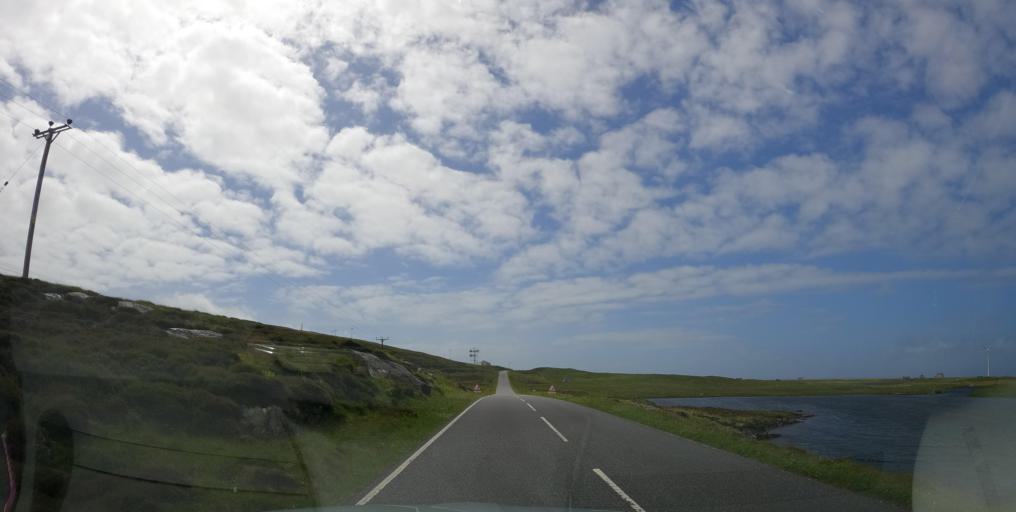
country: GB
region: Scotland
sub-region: Eilean Siar
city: Isle of South Uist
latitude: 57.2374
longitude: -7.3904
